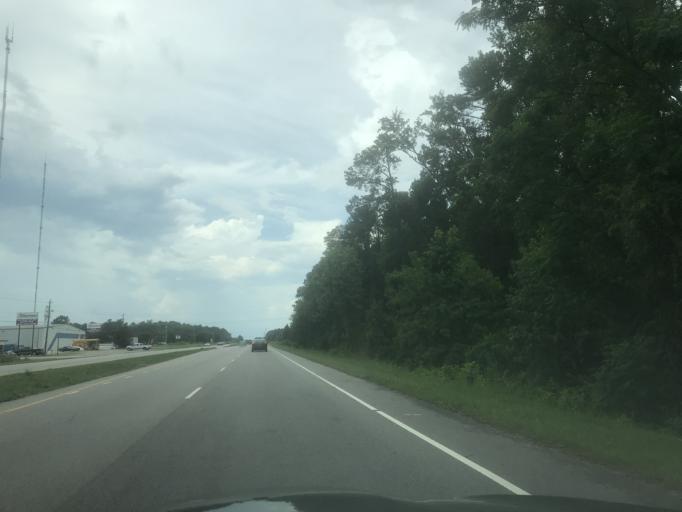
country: US
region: North Carolina
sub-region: Johnston County
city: Clayton
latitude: 35.6737
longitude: -78.5152
